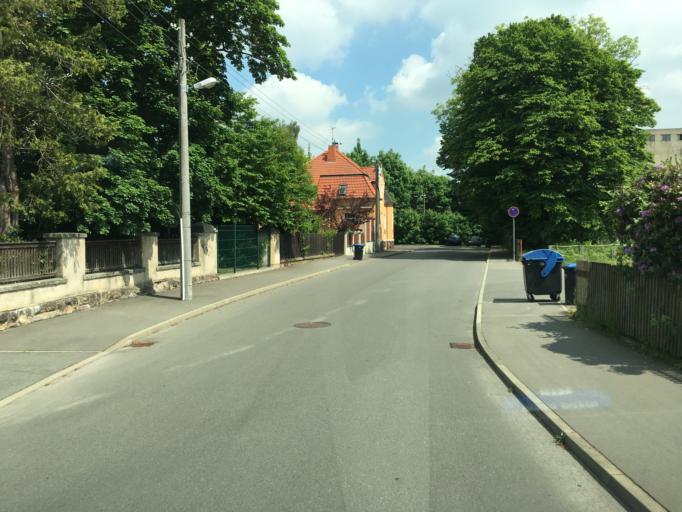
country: DE
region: Saxony
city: Hainichen
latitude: 50.9652
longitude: 13.1167
